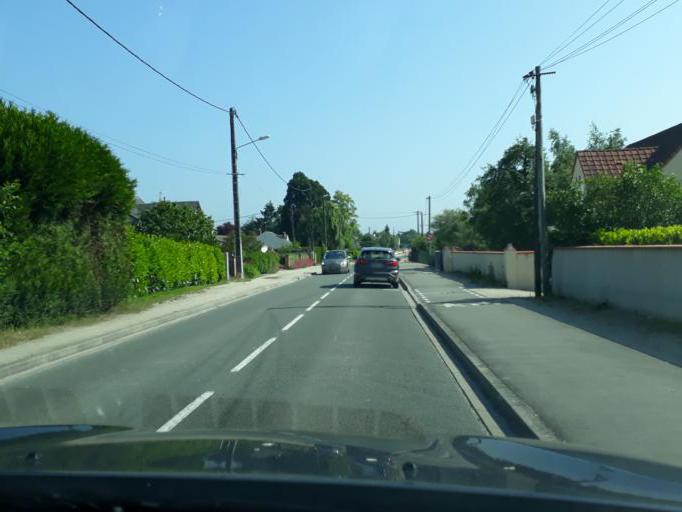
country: FR
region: Centre
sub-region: Departement du Loiret
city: Trainou
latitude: 47.9663
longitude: 2.0983
